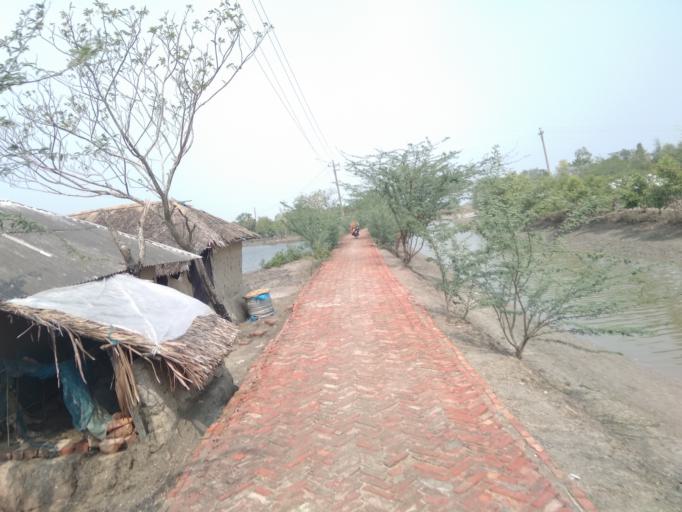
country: IN
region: West Bengal
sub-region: North 24 Parganas
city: Taki
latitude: 22.2795
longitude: 89.2844
